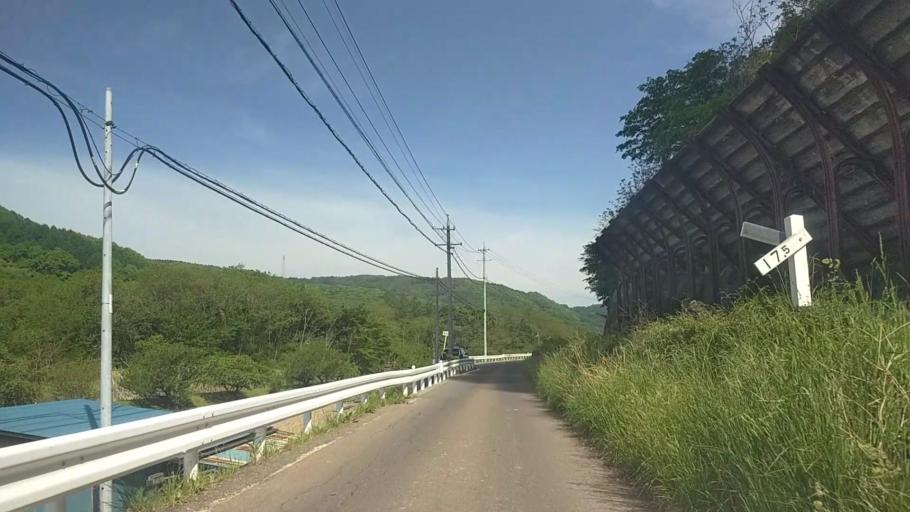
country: JP
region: Nagano
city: Saku
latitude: 36.1095
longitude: 138.4807
